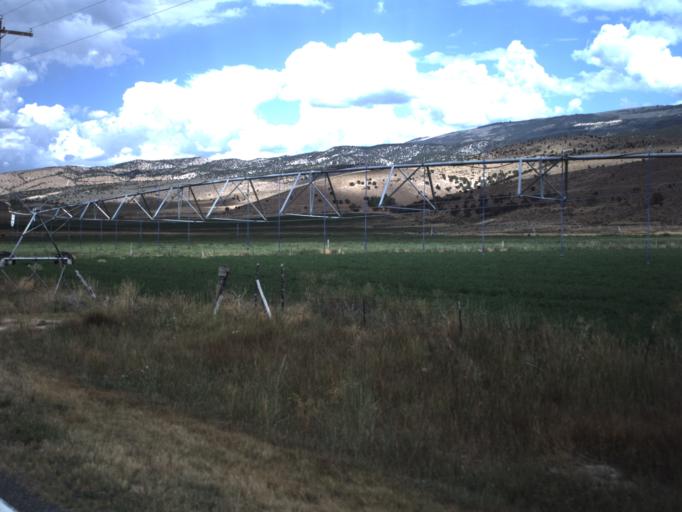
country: US
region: Utah
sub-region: Sanpete County
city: Centerfield
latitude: 39.1337
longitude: -111.7106
